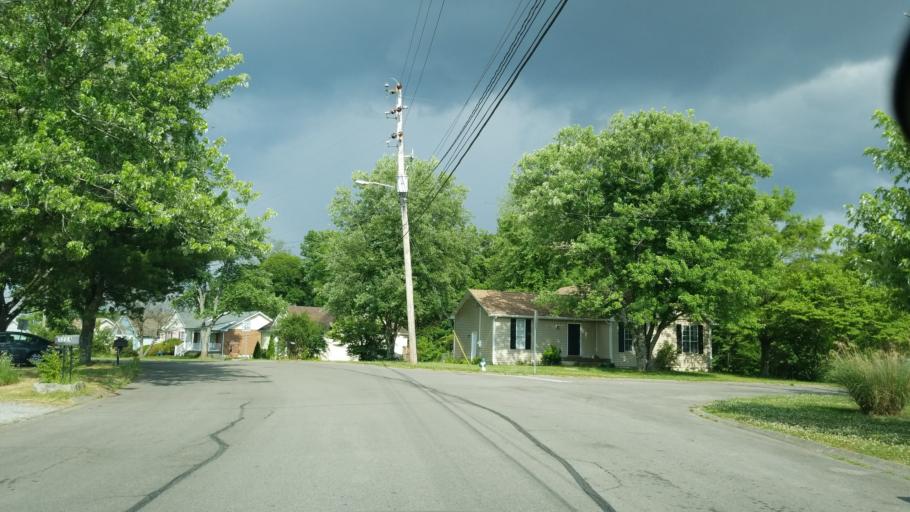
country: US
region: Tennessee
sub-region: Rutherford County
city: La Vergne
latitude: 36.0697
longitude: -86.6038
